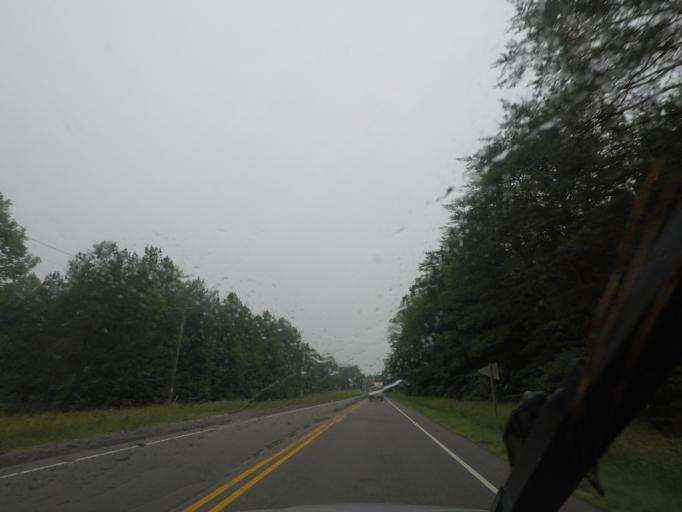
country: US
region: Virginia
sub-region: Buckingham County
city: Buckingham
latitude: 37.5011
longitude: -78.4779
